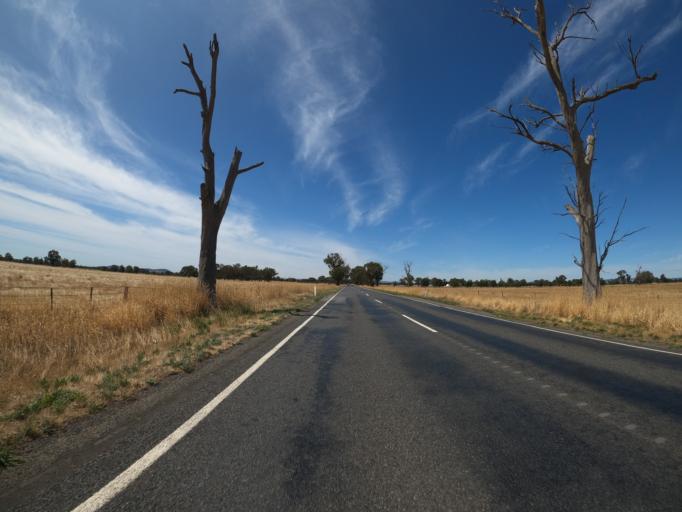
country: AU
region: Victoria
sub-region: Benalla
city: Benalla
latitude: -36.5116
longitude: 146.0292
